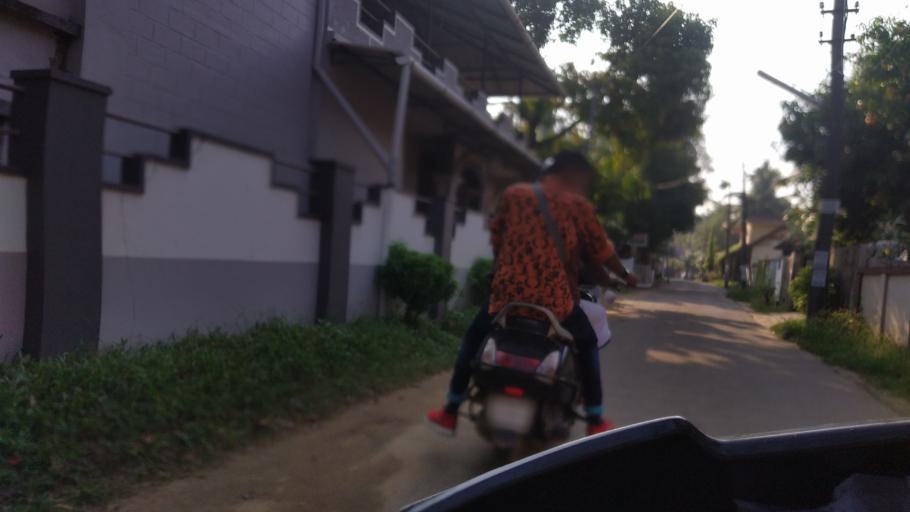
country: IN
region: Kerala
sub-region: Ernakulam
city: Elur
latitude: 10.0468
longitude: 76.2260
